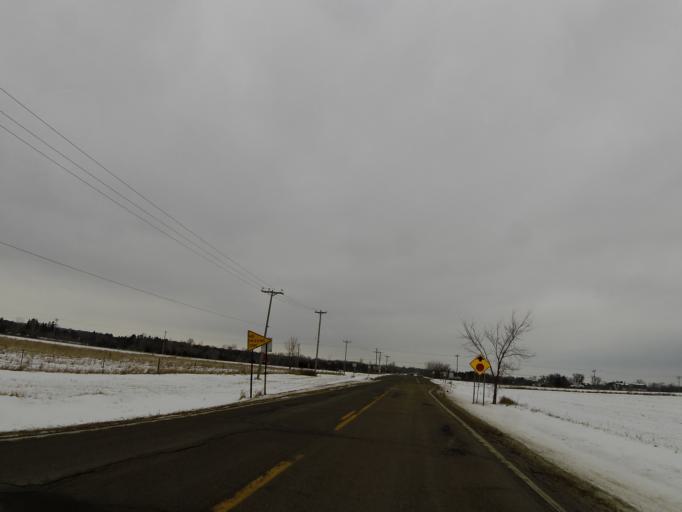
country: US
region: Minnesota
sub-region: Washington County
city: Lakeland
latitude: 44.9514
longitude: -92.7967
